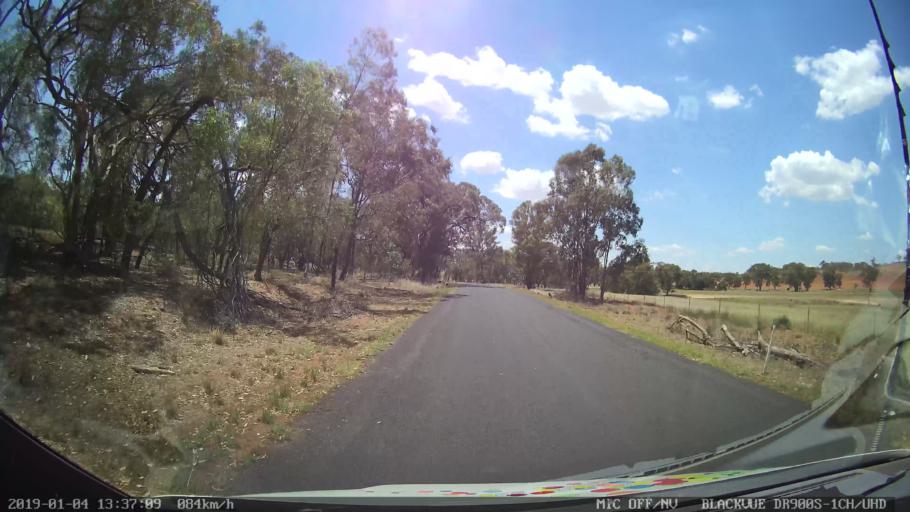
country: AU
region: New South Wales
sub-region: Dubbo Municipality
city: Dubbo
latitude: -32.5530
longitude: 148.5409
